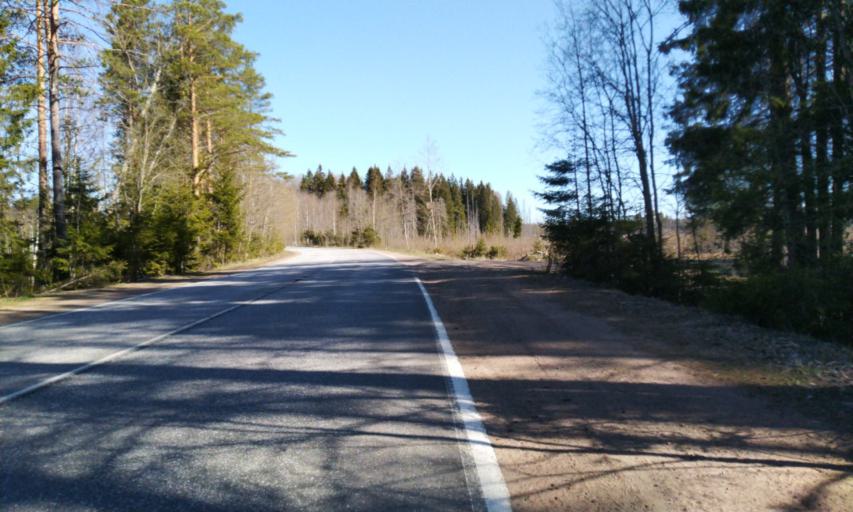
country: RU
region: Leningrad
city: Garbolovo
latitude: 60.3591
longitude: 30.4454
